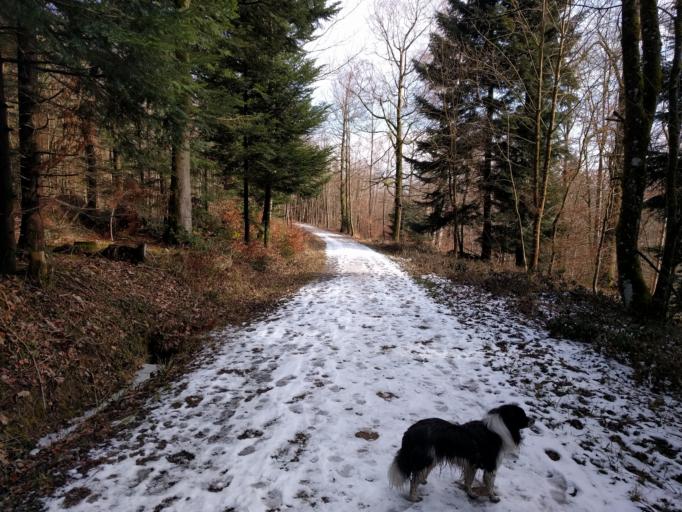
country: CH
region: Aargau
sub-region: Bezirk Aarau
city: Kuttigen
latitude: 47.4085
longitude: 8.0391
